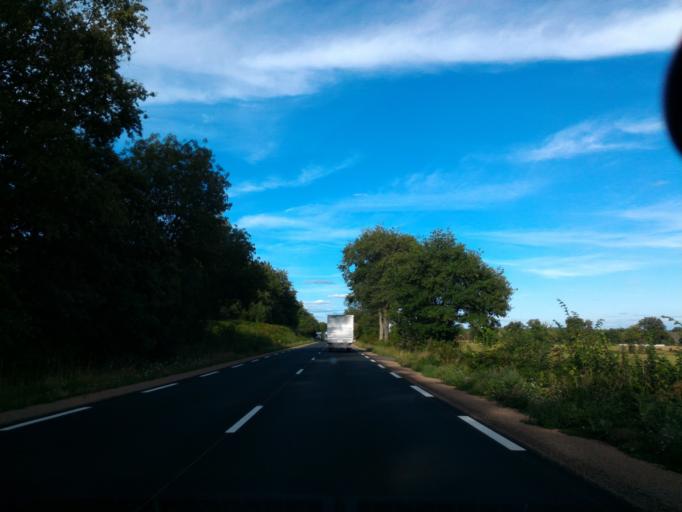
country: FR
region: Limousin
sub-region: Departement de la Haute-Vienne
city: Magnac-Laval
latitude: 46.1821
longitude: 1.1749
